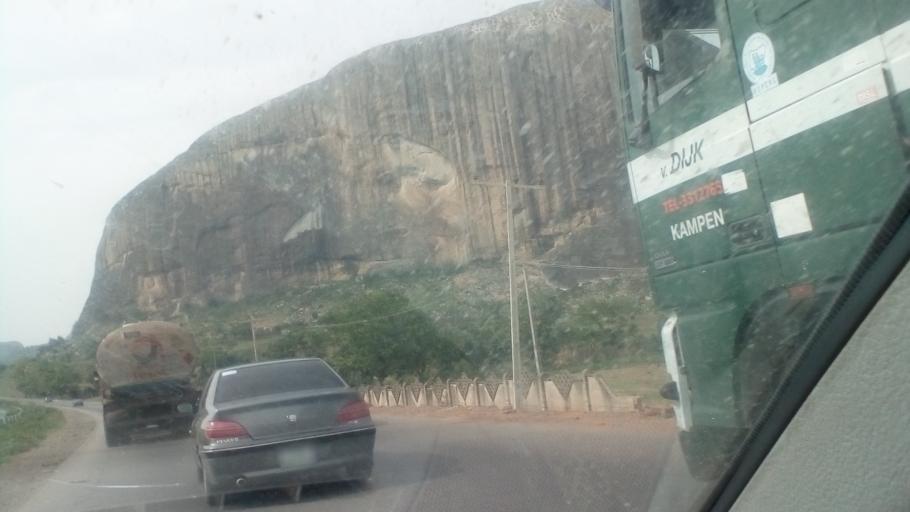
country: NG
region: Abuja Federal Capital Territory
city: Madala
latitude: 9.1232
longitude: 7.2287
